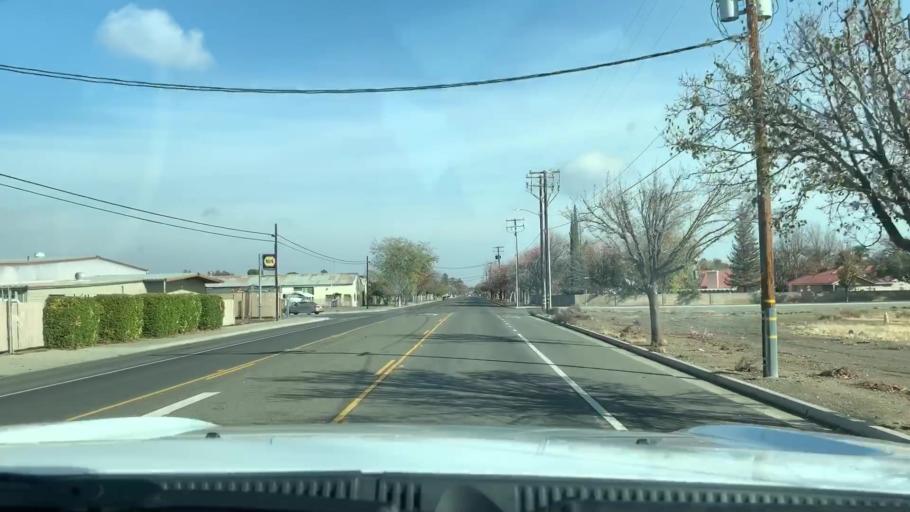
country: US
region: California
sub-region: Fresno County
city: Coalinga
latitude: 36.1304
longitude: -120.3691
